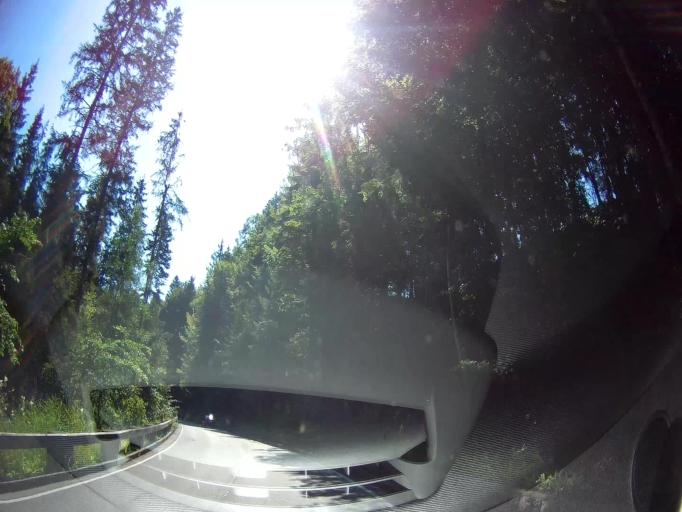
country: DE
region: Bavaria
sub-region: Upper Bavaria
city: Marktschellenberg
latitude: 47.6517
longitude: 13.0521
